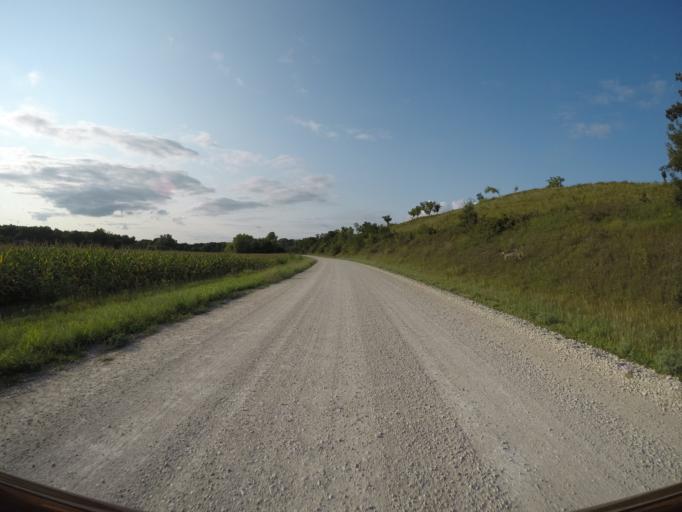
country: US
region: Kansas
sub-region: Wabaunsee County
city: Alma
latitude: 38.9721
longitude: -96.2627
